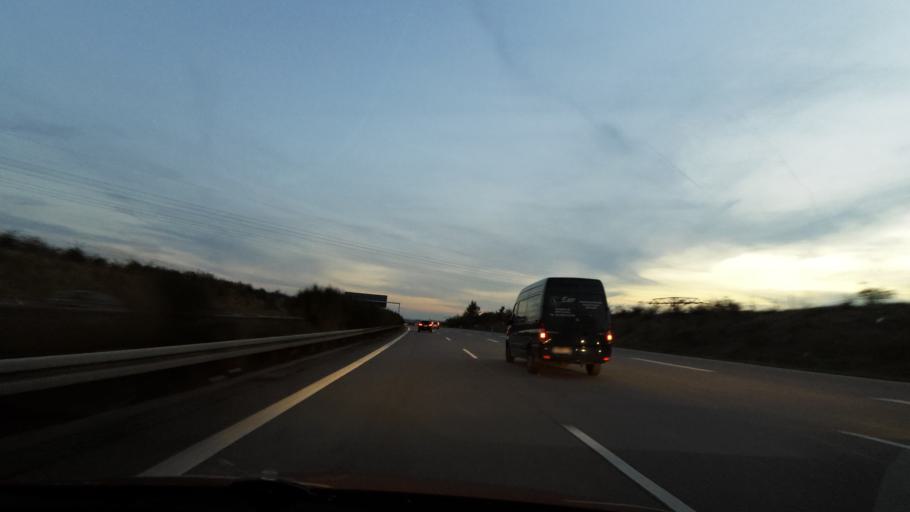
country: DE
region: Saxony-Anhalt
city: Ermlitz
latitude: 51.3973
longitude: 12.1810
